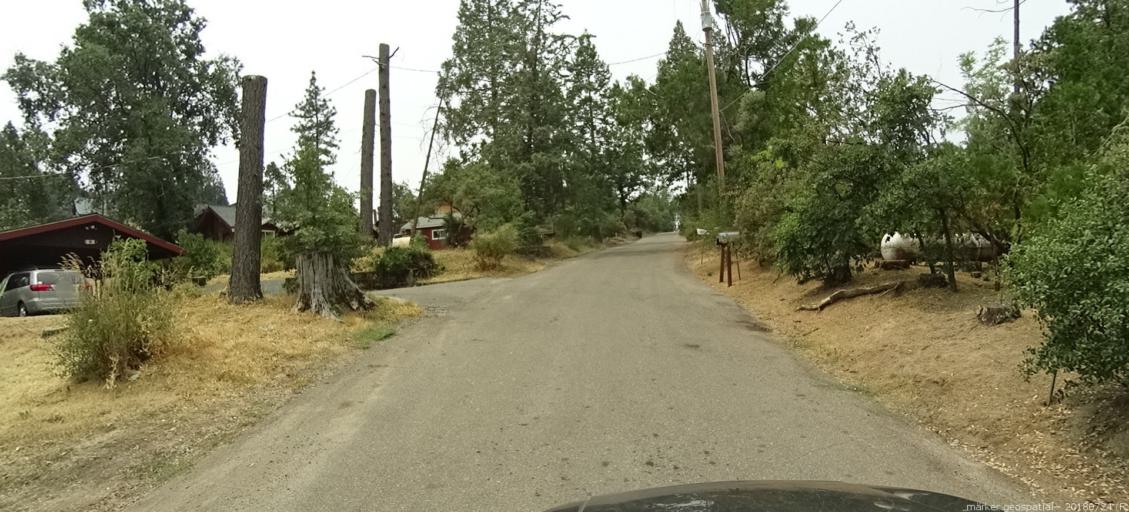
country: US
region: California
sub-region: Madera County
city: Oakhurst
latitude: 37.3192
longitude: -119.5835
